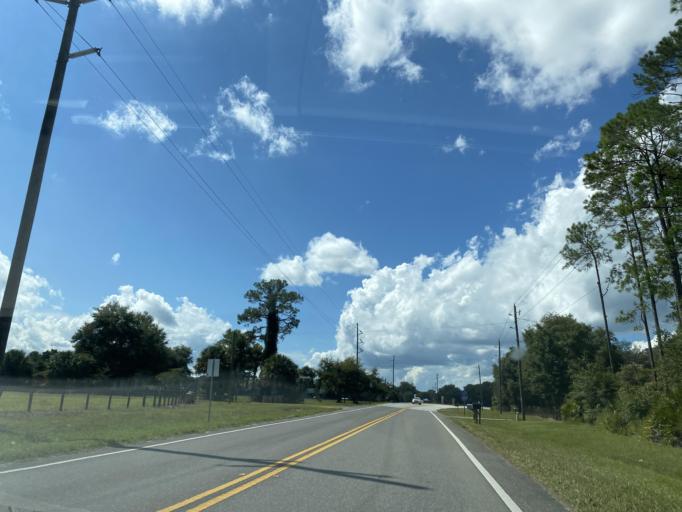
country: US
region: Florida
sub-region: Lake County
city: Umatilla
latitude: 28.9603
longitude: -81.6246
